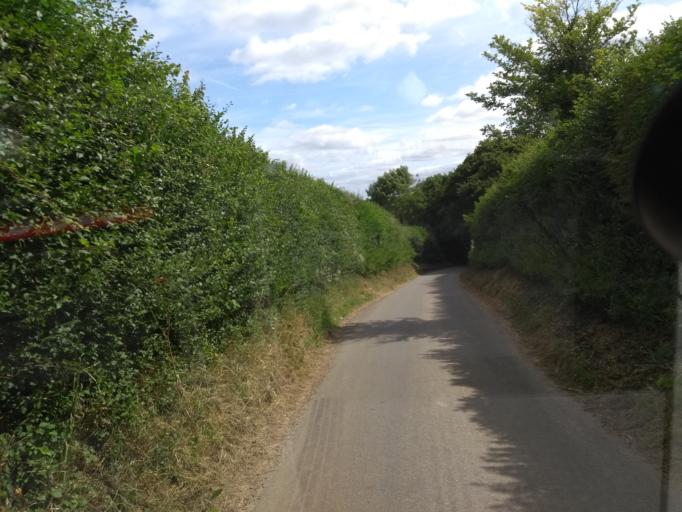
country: GB
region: England
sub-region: Somerset
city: Ilminster
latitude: 50.9274
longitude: -2.8627
